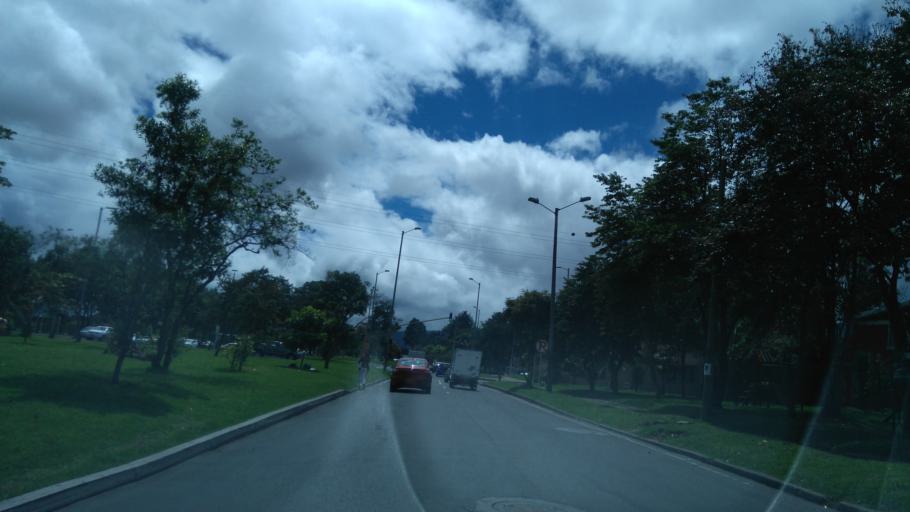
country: CO
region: Bogota D.C.
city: Bogota
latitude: 4.6513
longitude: -74.0939
